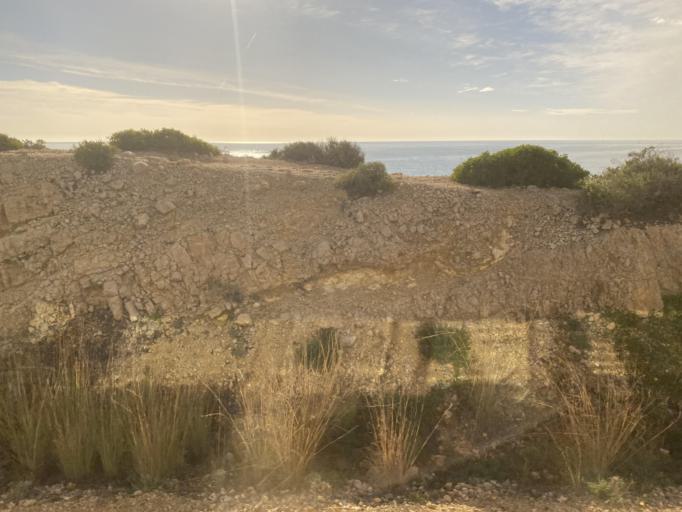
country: ES
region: Catalonia
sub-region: Provincia de Barcelona
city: Vilanova i la Geltru
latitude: 41.2200
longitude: 1.7557
